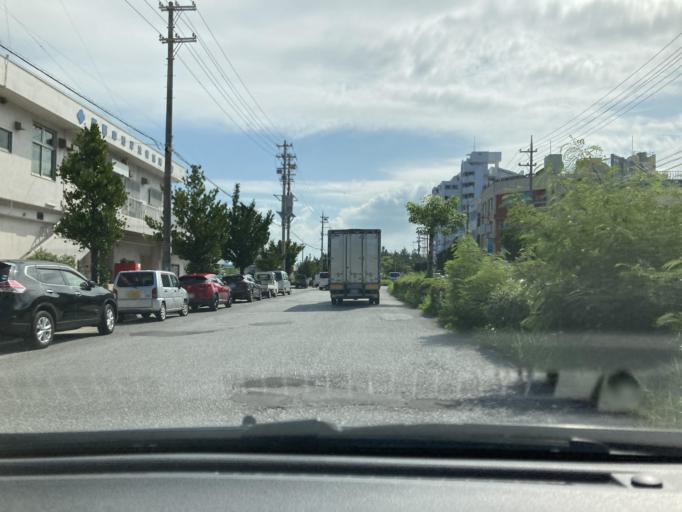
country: JP
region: Okinawa
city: Naha-shi
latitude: 26.2435
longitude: 127.6798
